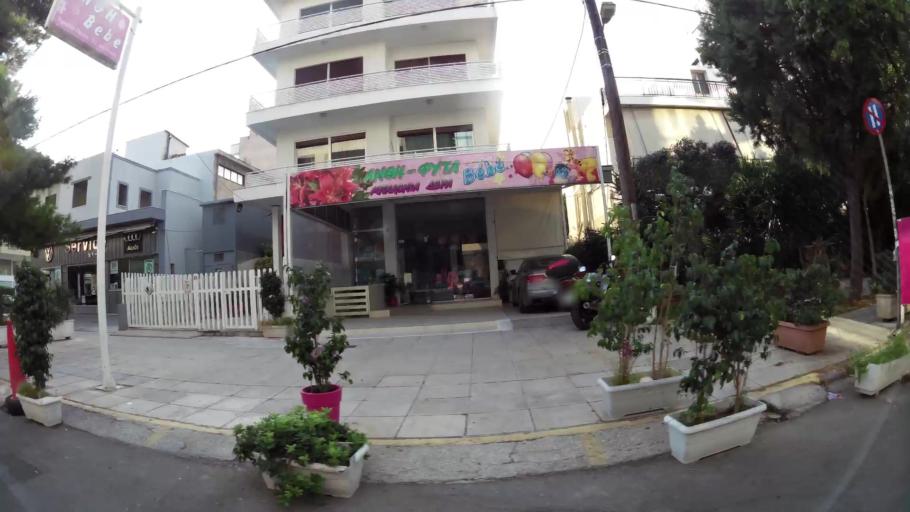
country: GR
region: Attica
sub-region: Nomarchia Athinas
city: Kallithea
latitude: 37.9407
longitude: 23.6980
